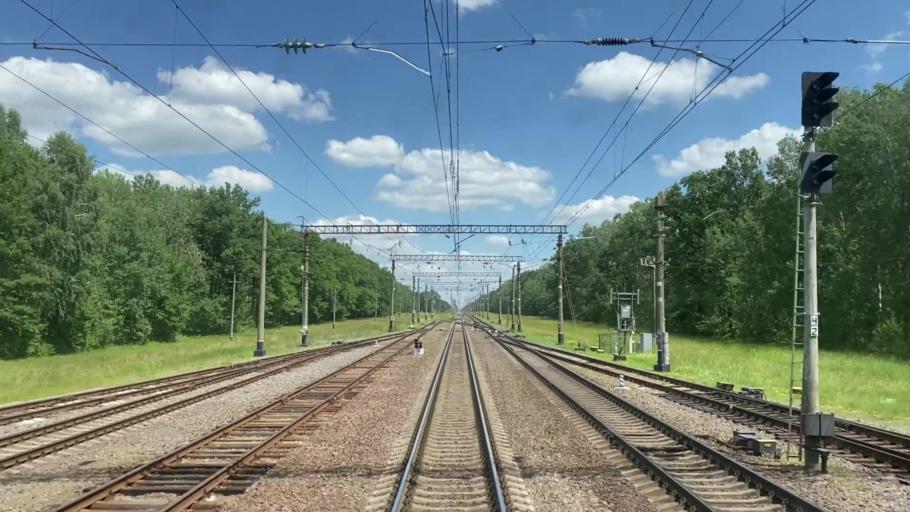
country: BY
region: Brest
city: Pruzhany
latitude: 52.4778
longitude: 24.5465
